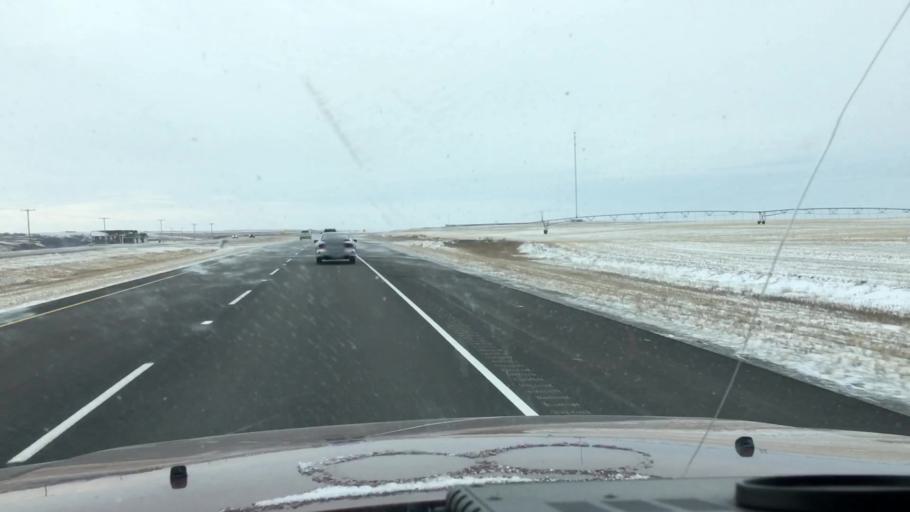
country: CA
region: Saskatchewan
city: Saskatoon
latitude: 51.7448
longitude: -106.4764
